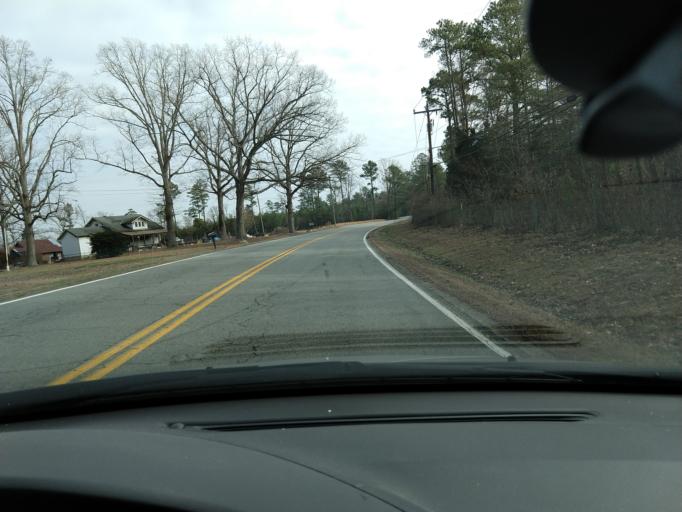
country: US
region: Virginia
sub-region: Henrico County
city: Fort Lee
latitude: 37.4464
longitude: -77.2413
